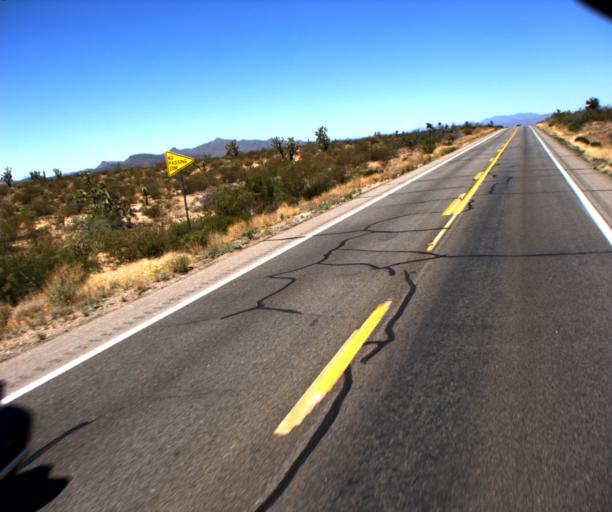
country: US
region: Arizona
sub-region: Yavapai County
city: Congress
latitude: 34.2440
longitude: -113.0781
